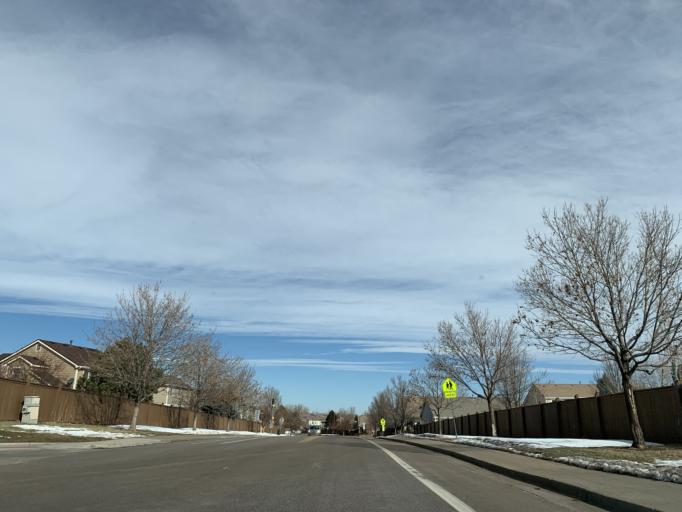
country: US
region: Colorado
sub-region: Douglas County
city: Carriage Club
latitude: 39.5277
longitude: -104.9332
